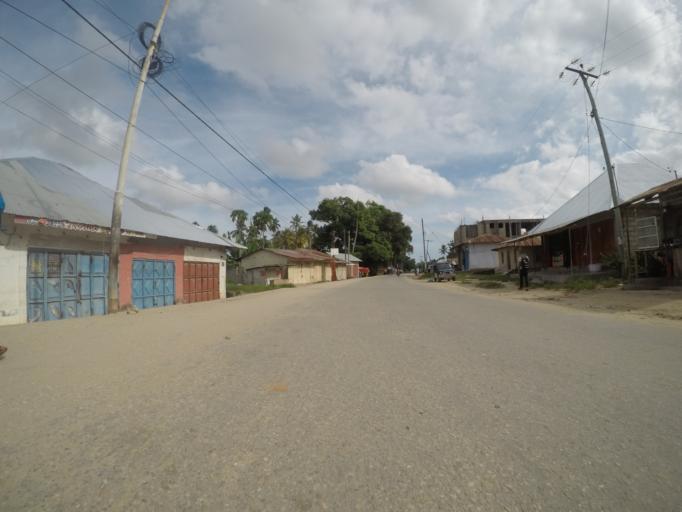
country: TZ
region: Pemba South
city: Chake Chake
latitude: -5.2368
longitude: 39.7794
